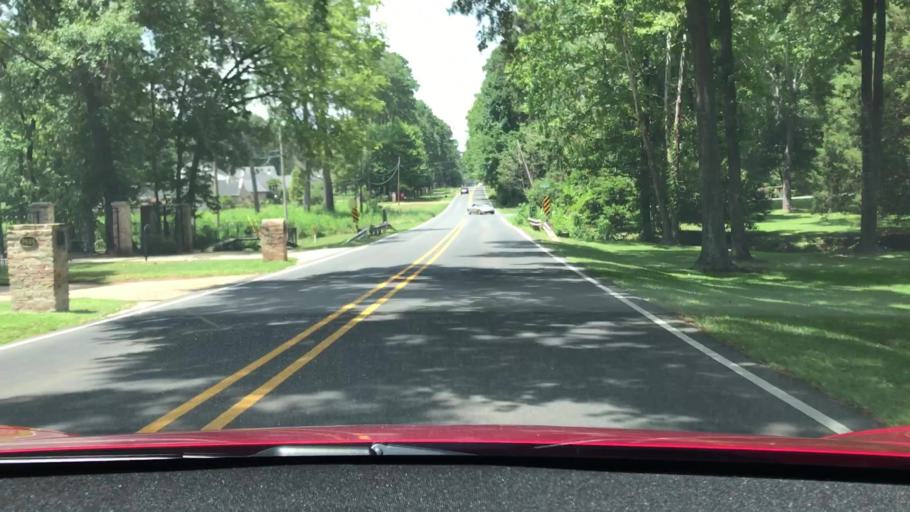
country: US
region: Louisiana
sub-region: Bossier Parish
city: Bossier City
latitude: 32.3769
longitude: -93.7137
